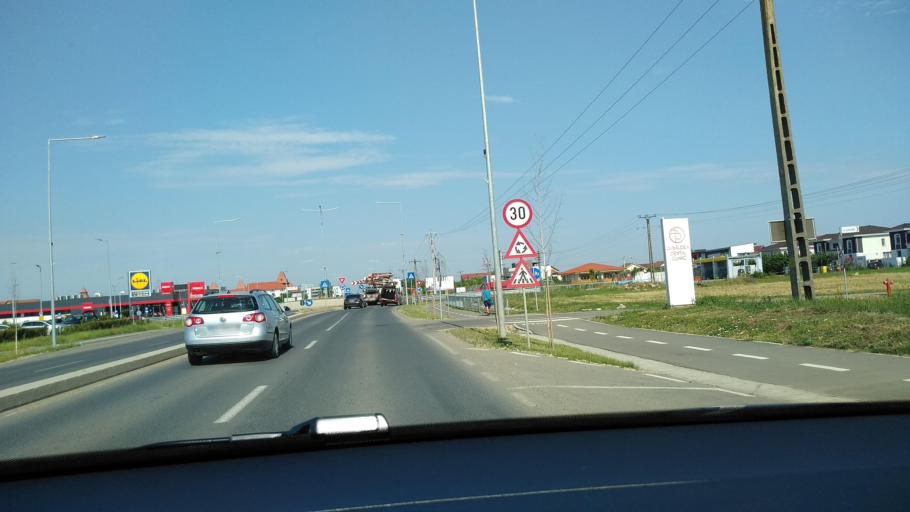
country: RO
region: Timis
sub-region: Comuna Mosnita Noua
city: Mosnita Noua
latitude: 45.7228
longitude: 21.3013
